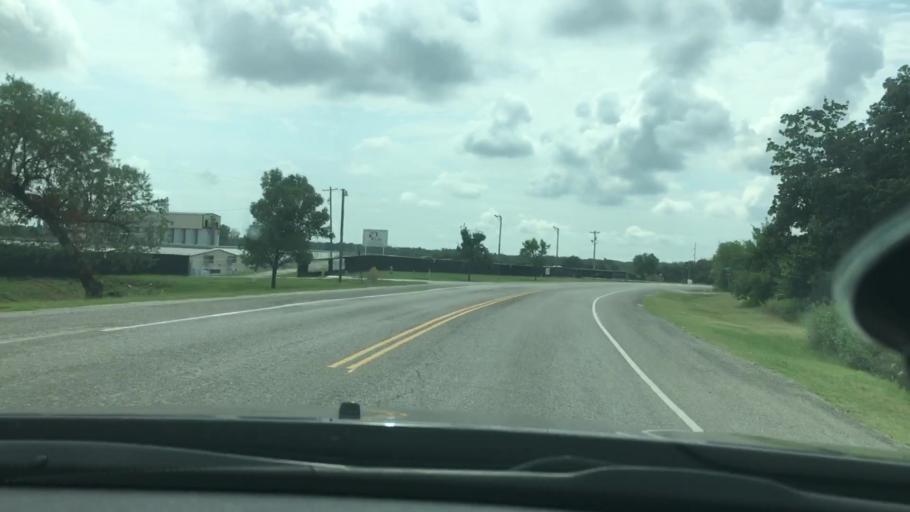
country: US
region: Oklahoma
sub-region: Carter County
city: Ardmore
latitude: 34.2008
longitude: -97.1089
